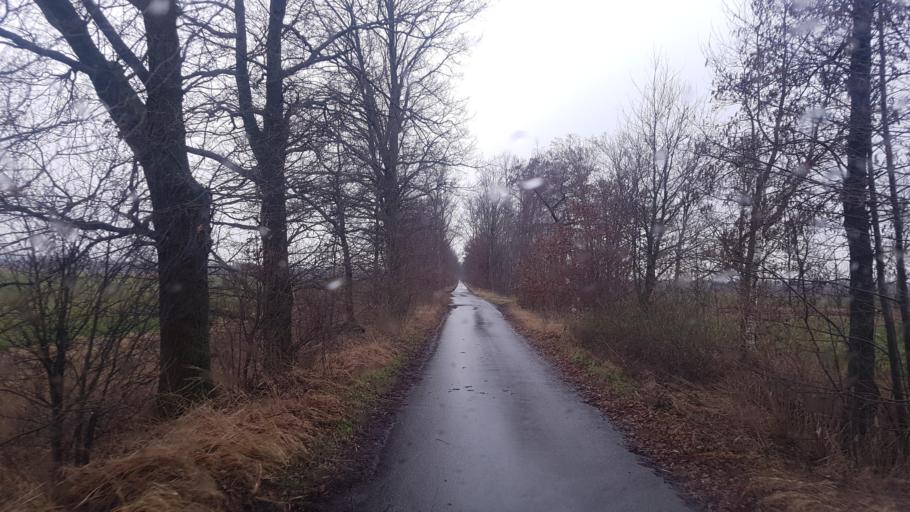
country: DE
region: Brandenburg
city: Grossthiemig
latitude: 51.4243
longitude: 13.6508
